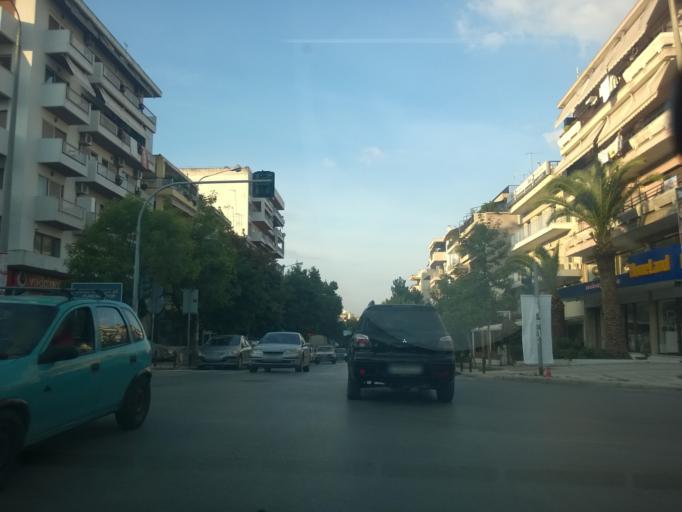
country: GR
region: Central Macedonia
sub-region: Nomos Thessalonikis
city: Kalamaria
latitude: 40.5895
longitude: 22.9599
